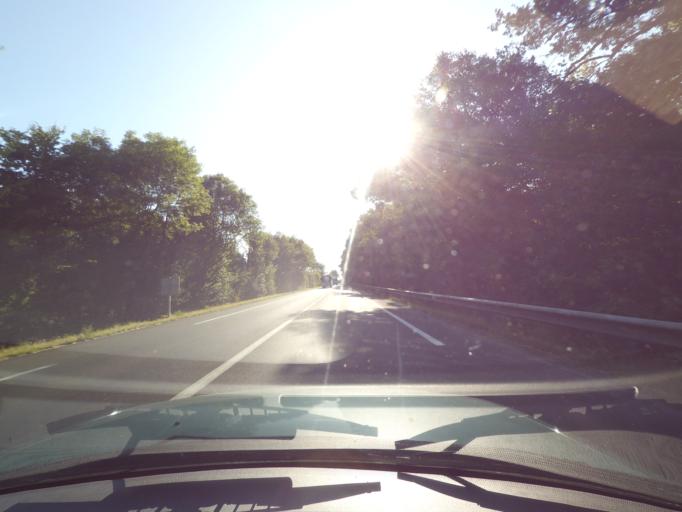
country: FR
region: Poitou-Charentes
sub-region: Departement des Deux-Sevres
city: La Peyratte
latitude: 46.6536
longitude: -0.1000
